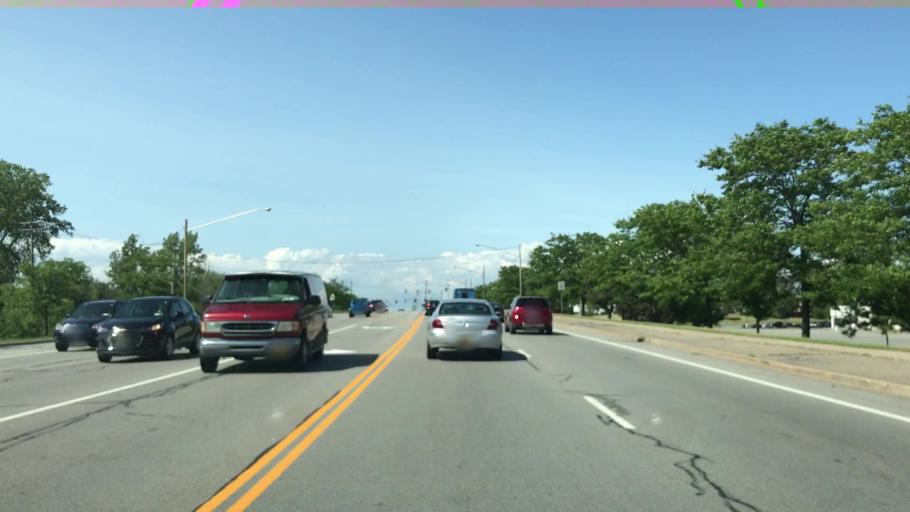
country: US
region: New York
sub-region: Erie County
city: Sloan
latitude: 42.9040
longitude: -78.7840
